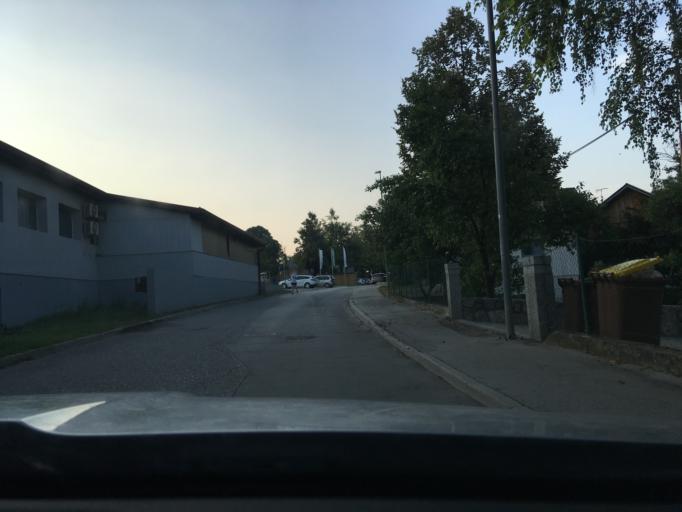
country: SI
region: Kocevje
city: Kocevje
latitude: 45.6434
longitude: 14.8715
